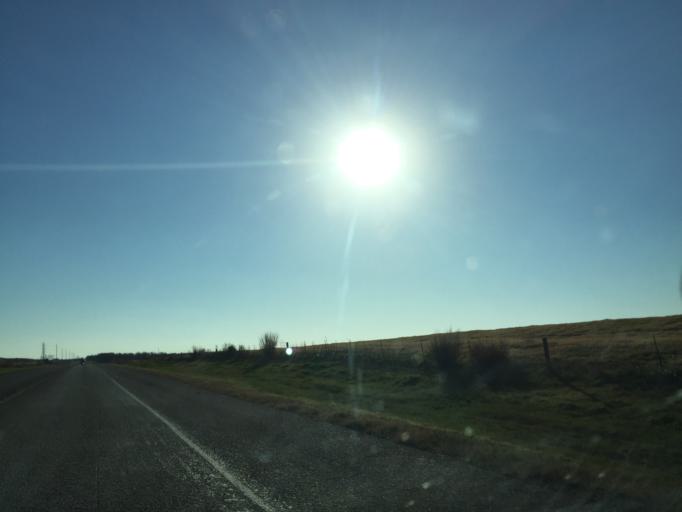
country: US
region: Texas
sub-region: Bastrop County
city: Elgin
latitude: 30.3459
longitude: -97.2773
